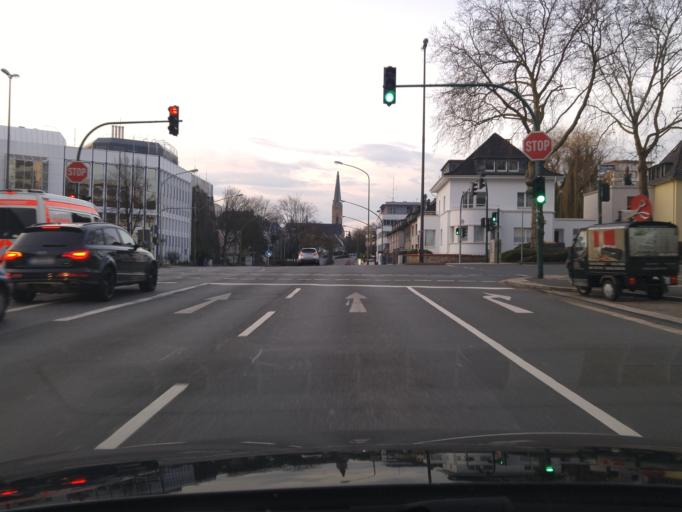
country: DE
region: North Rhine-Westphalia
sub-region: Regierungsbezirk Dusseldorf
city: Essen
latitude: 51.4431
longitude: 7.0340
